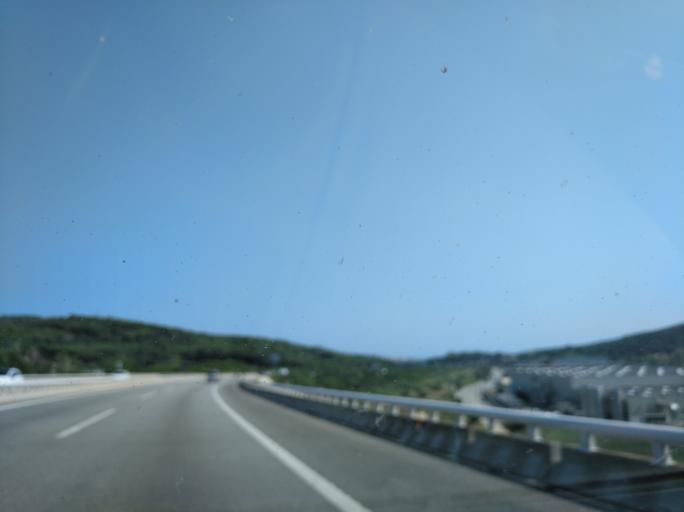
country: ES
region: Catalonia
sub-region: Provincia de Barcelona
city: Argentona
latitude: 41.5718
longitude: 2.3922
